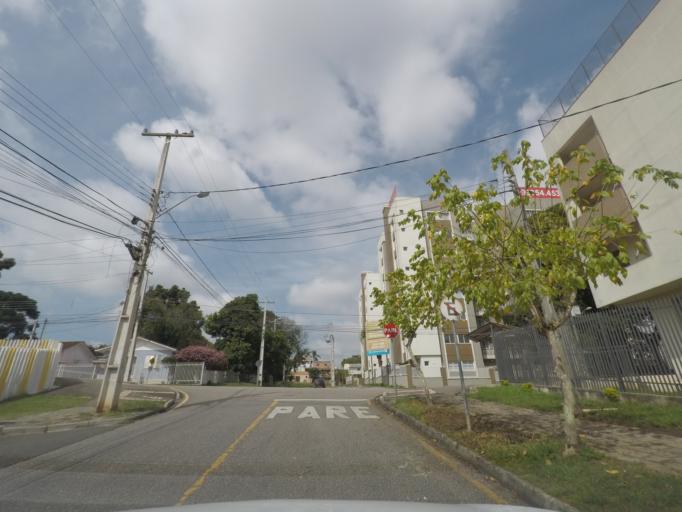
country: BR
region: Parana
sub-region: Curitiba
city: Curitiba
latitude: -25.4750
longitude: -49.2864
